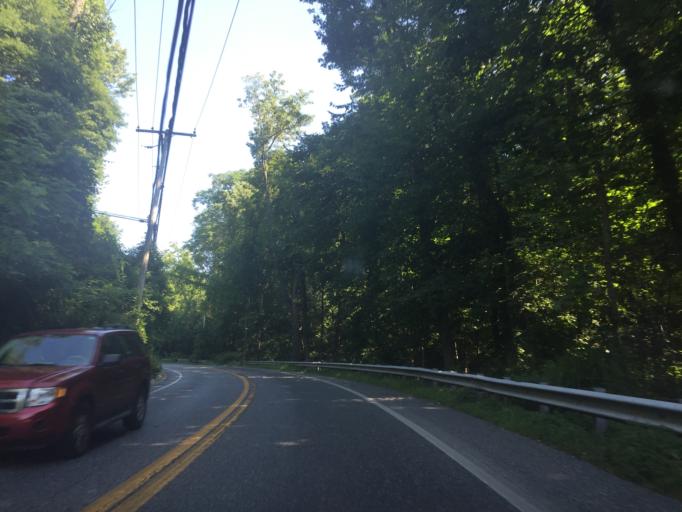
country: US
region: Maryland
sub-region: Baltimore County
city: Lutherville
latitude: 39.3796
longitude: -76.6514
